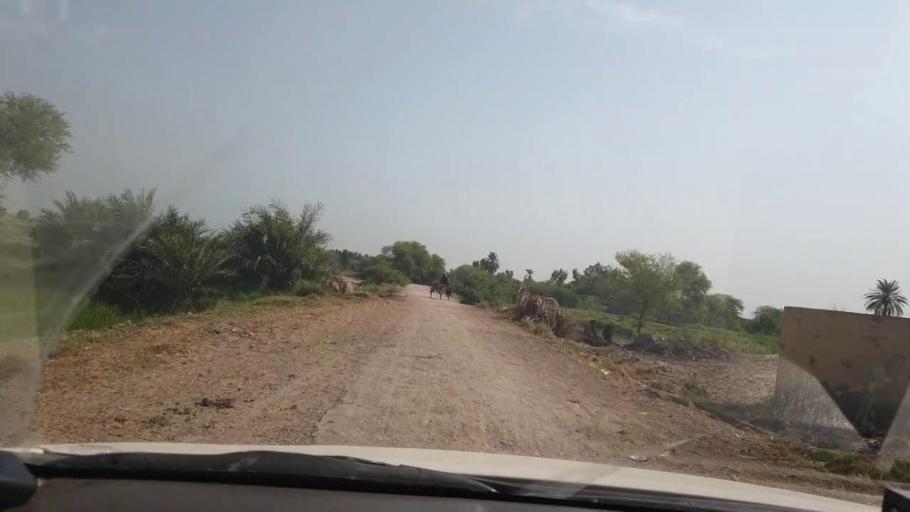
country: PK
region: Sindh
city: Chak
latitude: 27.8284
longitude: 68.7984
